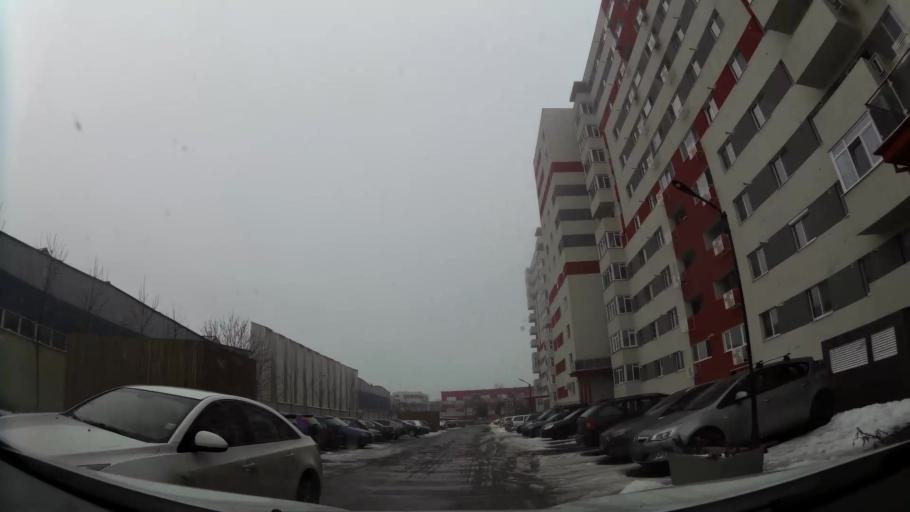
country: RO
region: Ilfov
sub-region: Comuna Chiajna
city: Rosu
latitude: 44.4359
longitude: 25.9997
